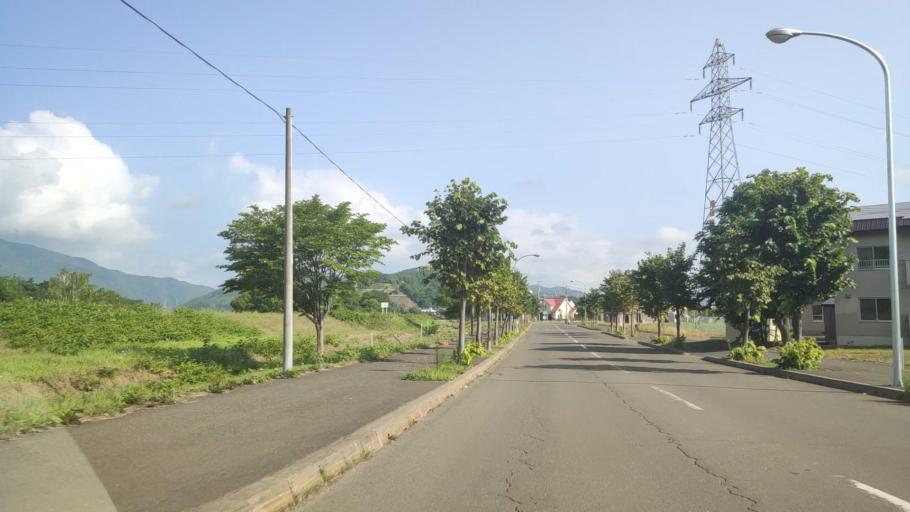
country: JP
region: Hokkaido
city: Shimo-furano
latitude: 43.3460
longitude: 142.3763
